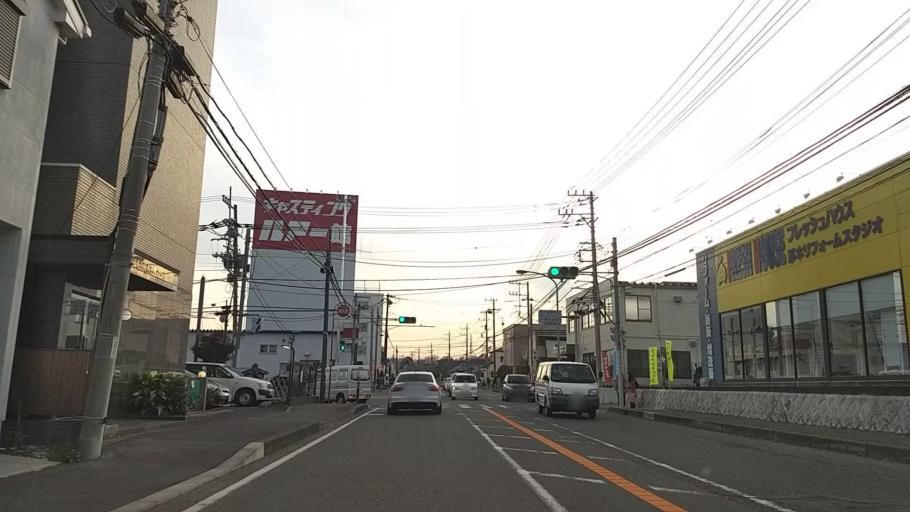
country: JP
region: Kanagawa
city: Atsugi
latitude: 35.4402
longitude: 139.3538
